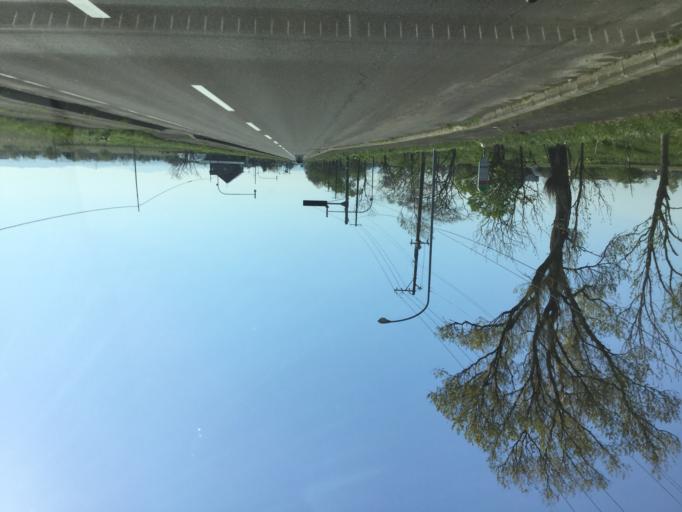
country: JP
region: Hokkaido
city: Ebetsu
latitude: 43.0543
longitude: 141.6475
